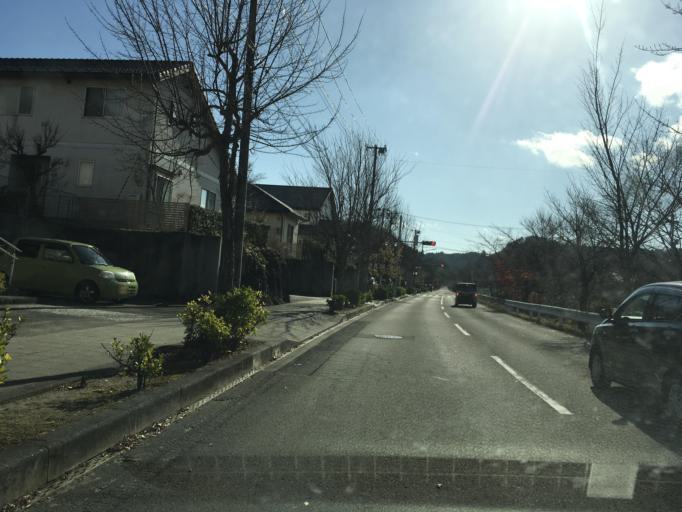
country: JP
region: Miyagi
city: Sendai
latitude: 38.2549
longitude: 140.7644
